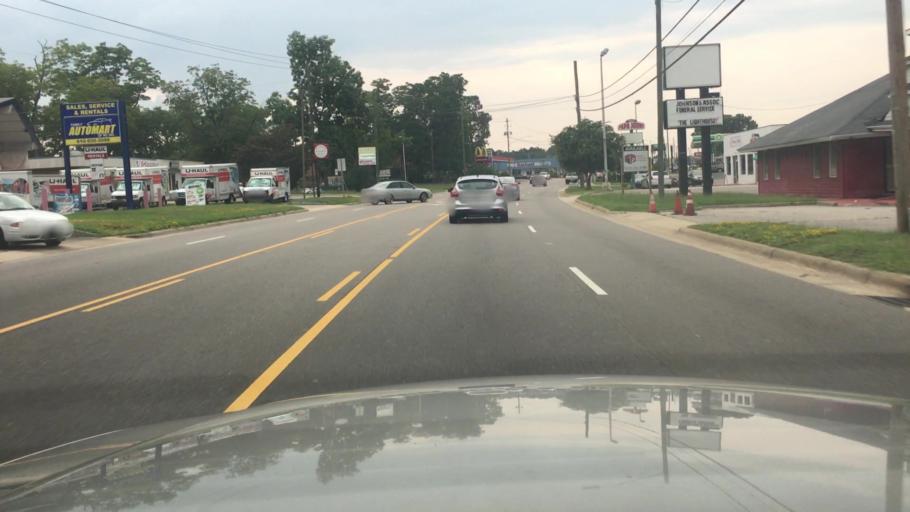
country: US
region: North Carolina
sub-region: Cumberland County
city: Fort Bragg
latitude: 35.0883
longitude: -78.9809
